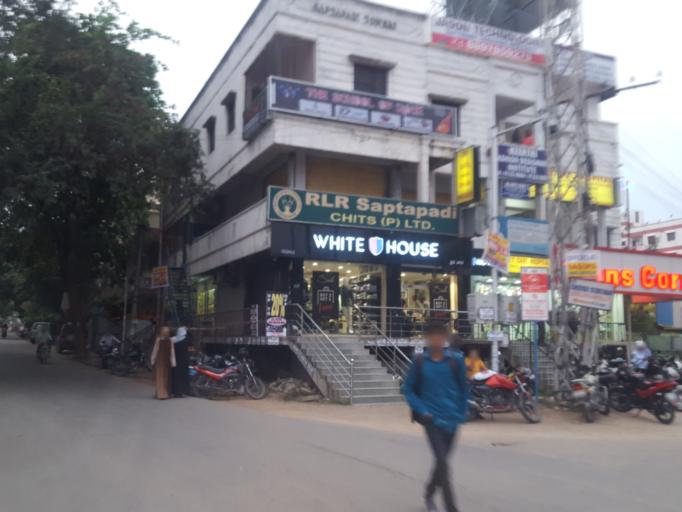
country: IN
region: Telangana
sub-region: Medak
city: Serilingampalle
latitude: 17.4950
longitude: 78.3324
